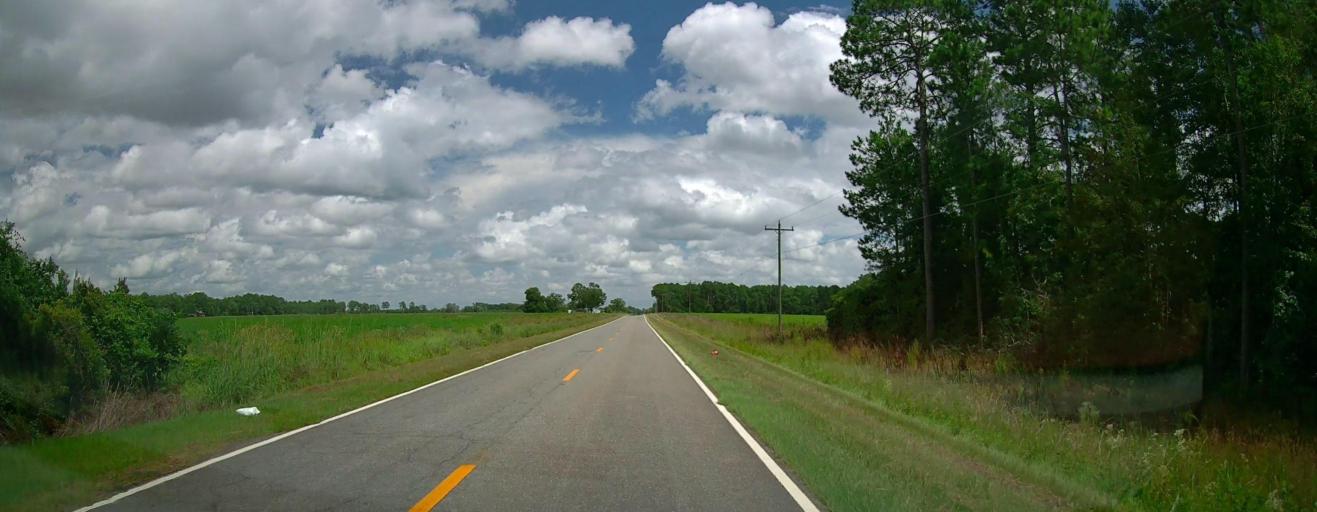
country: US
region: Georgia
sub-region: Irwin County
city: Ocilla
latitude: 31.6467
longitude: -83.2966
